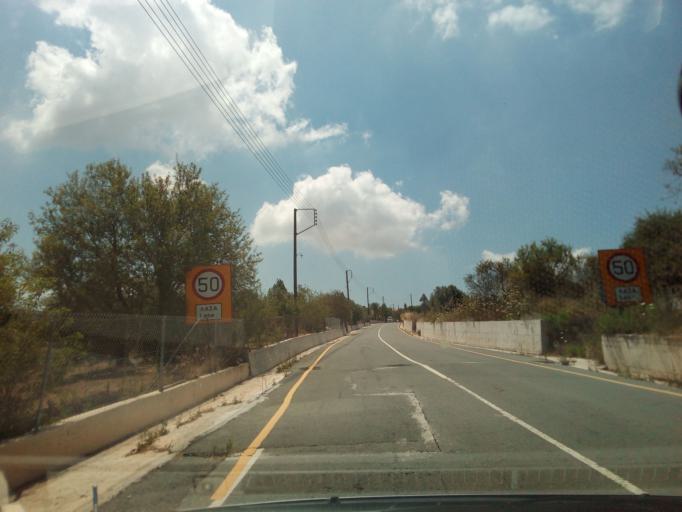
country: CY
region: Pafos
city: Tala
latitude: 34.9289
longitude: 32.5226
